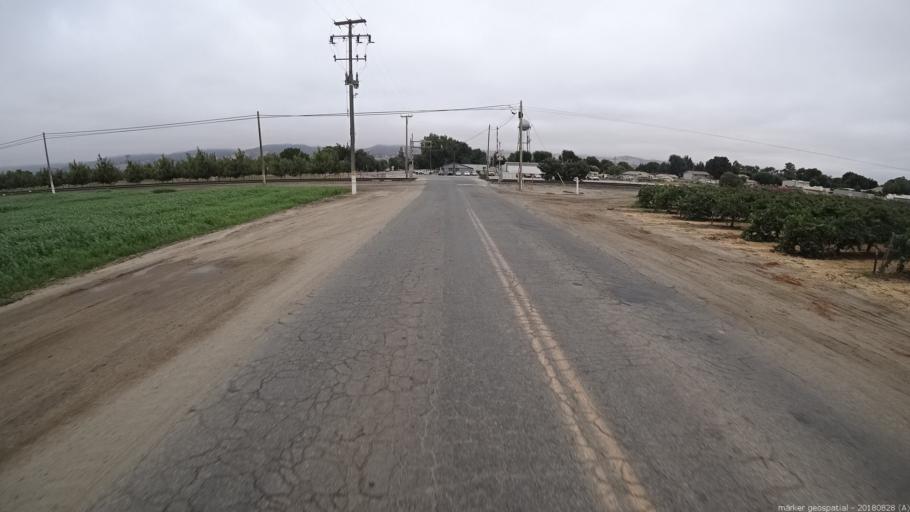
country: US
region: California
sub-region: San Luis Obispo County
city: Lake Nacimiento
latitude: 36.0207
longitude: -120.9003
